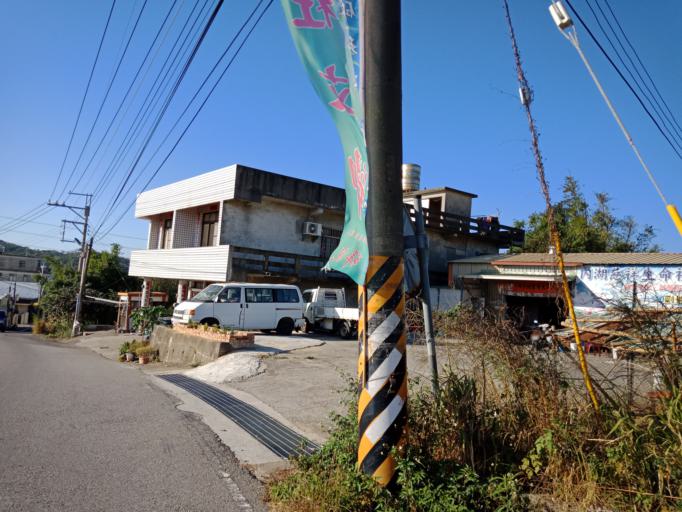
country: TW
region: Taiwan
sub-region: Miaoli
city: Miaoli
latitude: 24.4927
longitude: 120.6947
